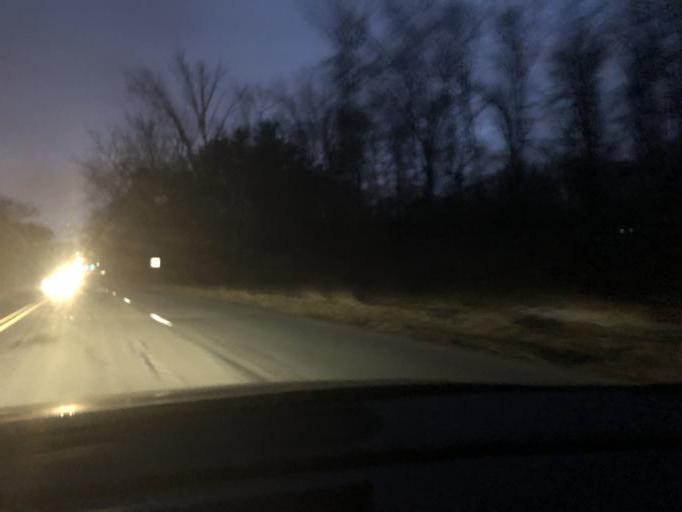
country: US
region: New Jersey
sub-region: Essex County
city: Short Hills
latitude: 40.7611
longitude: -74.3256
